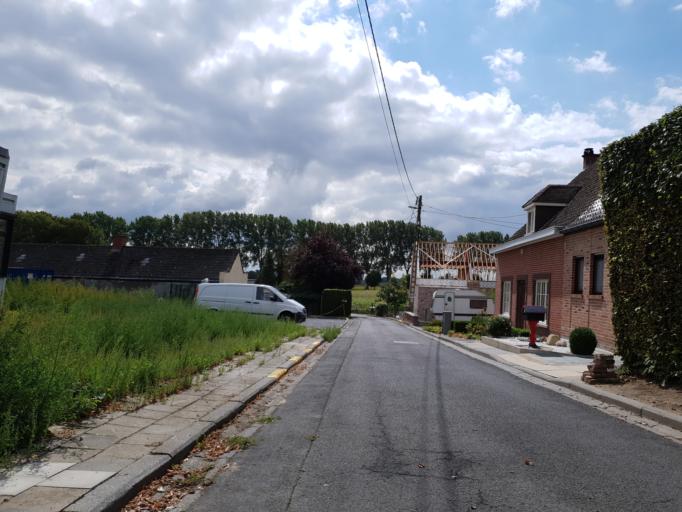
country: BE
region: Flanders
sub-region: Provincie West-Vlaanderen
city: Avelgem
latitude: 50.7478
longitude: 3.4103
